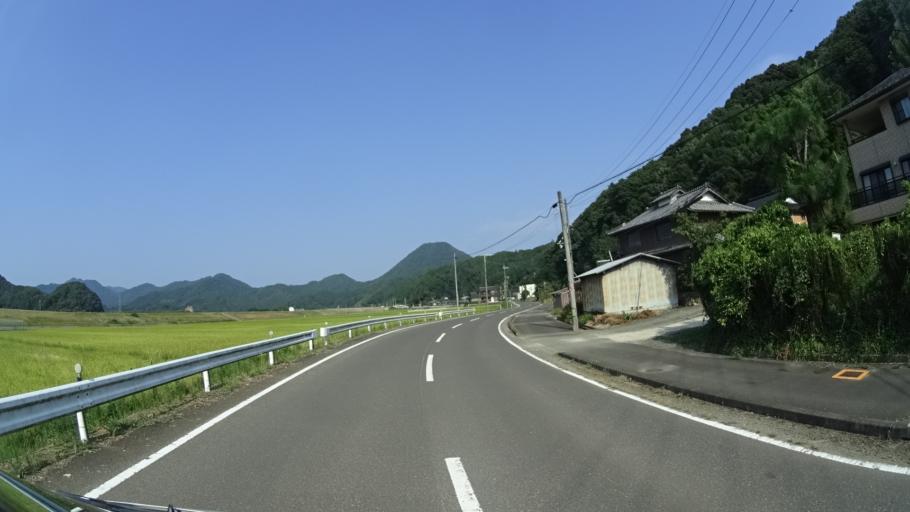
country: JP
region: Kyoto
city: Maizuru
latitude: 35.4543
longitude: 135.2733
